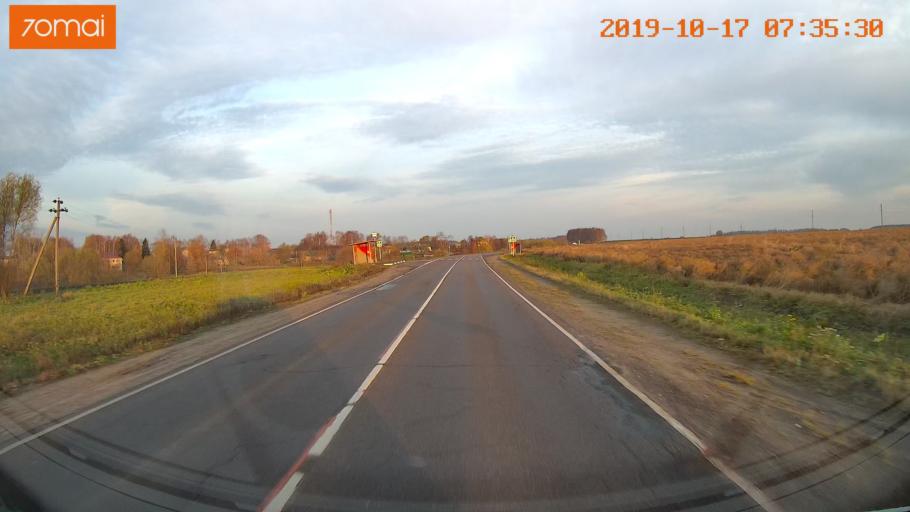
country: RU
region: Ivanovo
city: Gavrilov Posad
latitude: 56.4286
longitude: 39.9274
